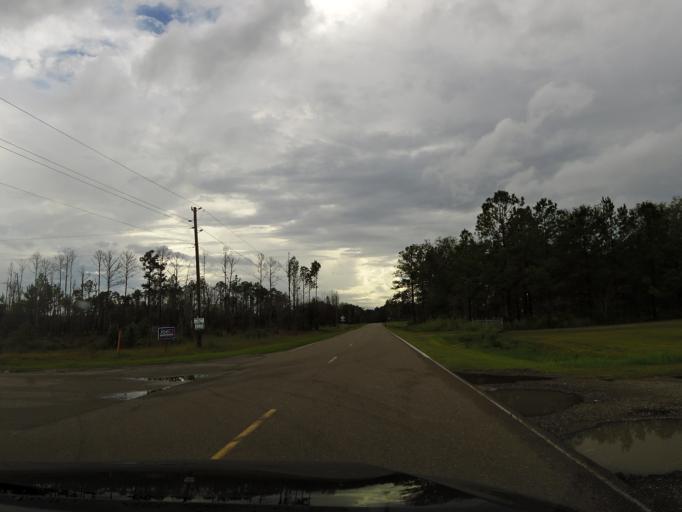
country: US
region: Florida
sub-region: Duval County
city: Baldwin
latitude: 30.4118
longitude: -82.0291
